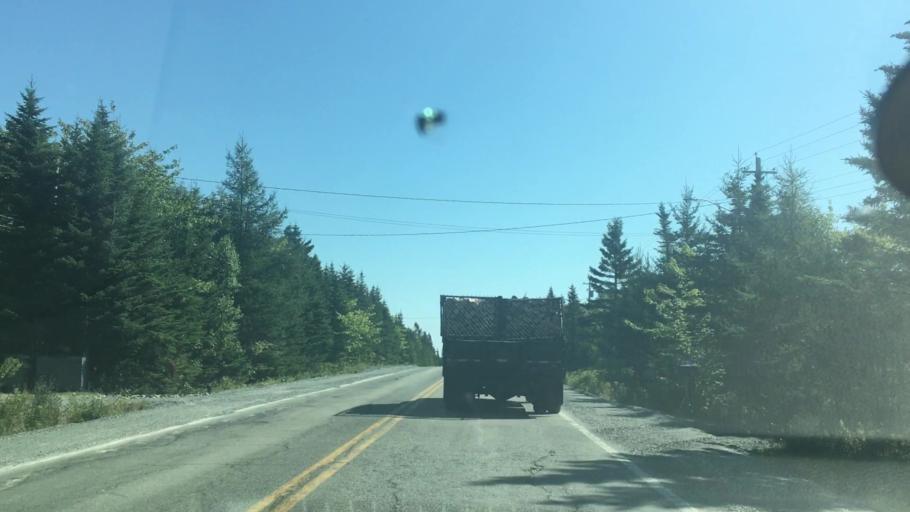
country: CA
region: Nova Scotia
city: New Glasgow
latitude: 44.9049
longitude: -62.4699
